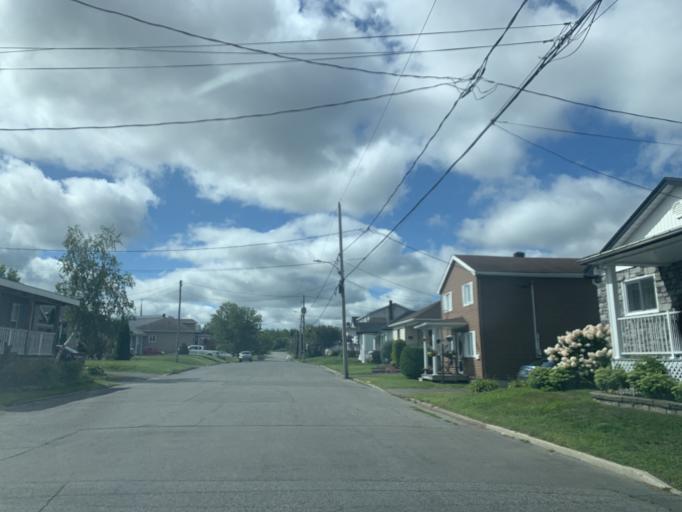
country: CA
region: Ontario
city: Hawkesbury
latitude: 45.6076
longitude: -74.5907
